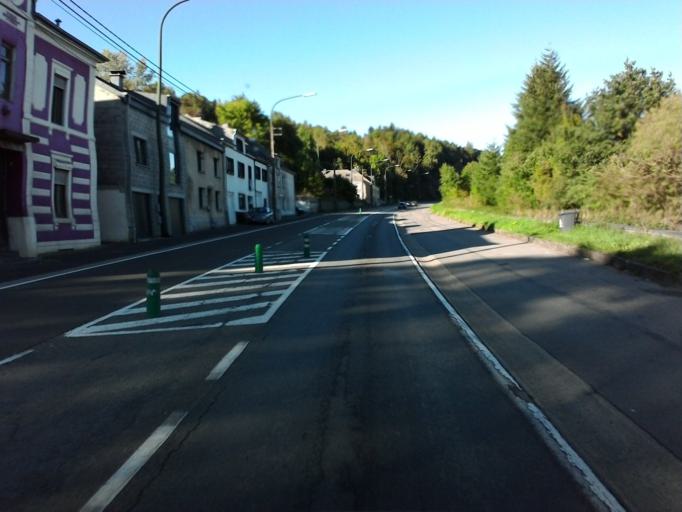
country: BE
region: Wallonia
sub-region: Province du Luxembourg
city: Martelange
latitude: 49.8361
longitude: 5.7383
